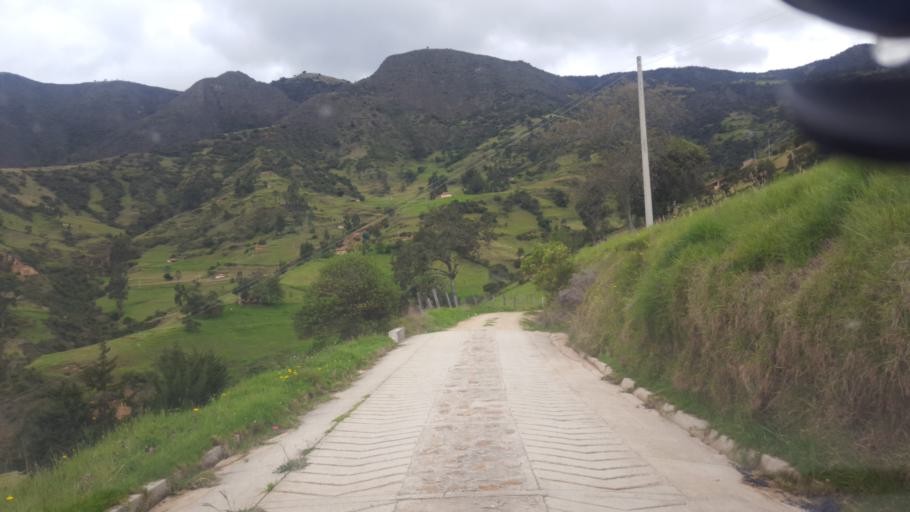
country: CO
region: Boyaca
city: Belen
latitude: 6.0161
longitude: -72.8773
